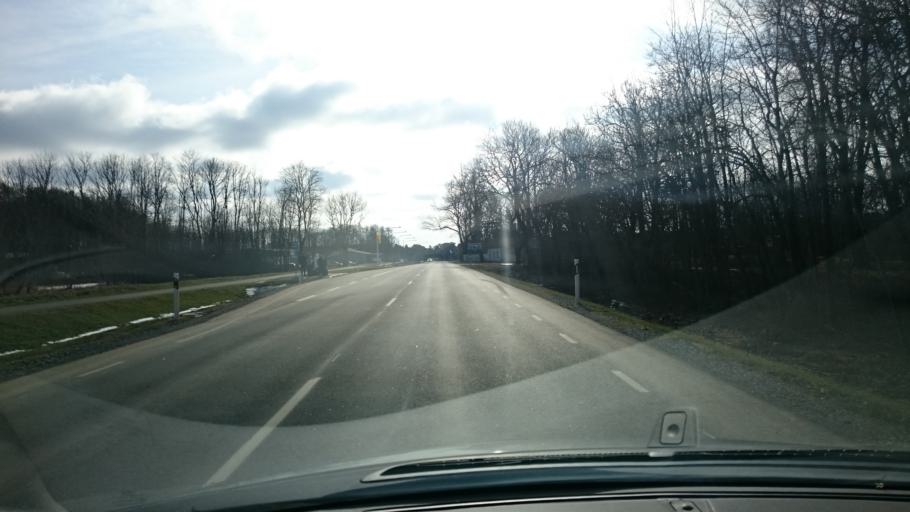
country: EE
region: Harju
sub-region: Paldiski linn
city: Paldiski
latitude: 59.3802
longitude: 24.2370
